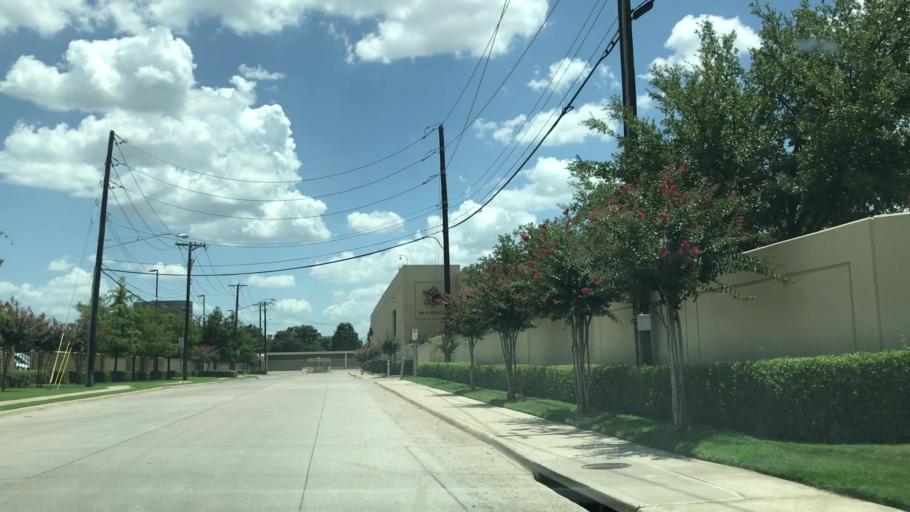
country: US
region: Texas
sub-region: Dallas County
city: Dallas
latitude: 32.8192
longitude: -96.8515
